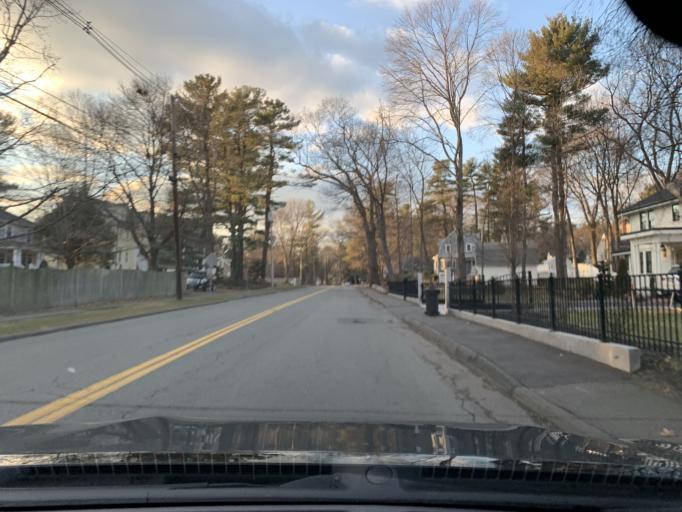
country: US
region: Massachusetts
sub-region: Essex County
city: Lynnfield
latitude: 42.5288
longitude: -71.0357
